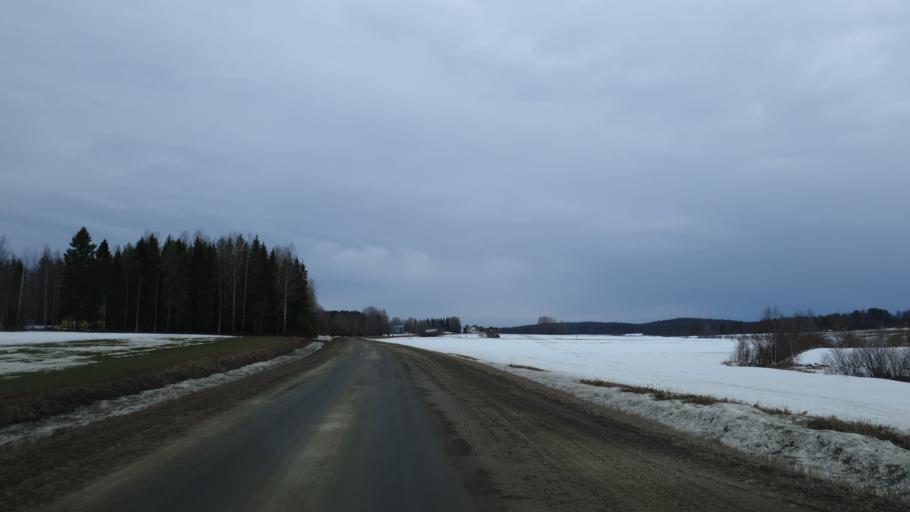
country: SE
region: Vaesterbotten
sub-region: Skelleftea Kommun
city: Burea
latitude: 64.3258
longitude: 21.1379
